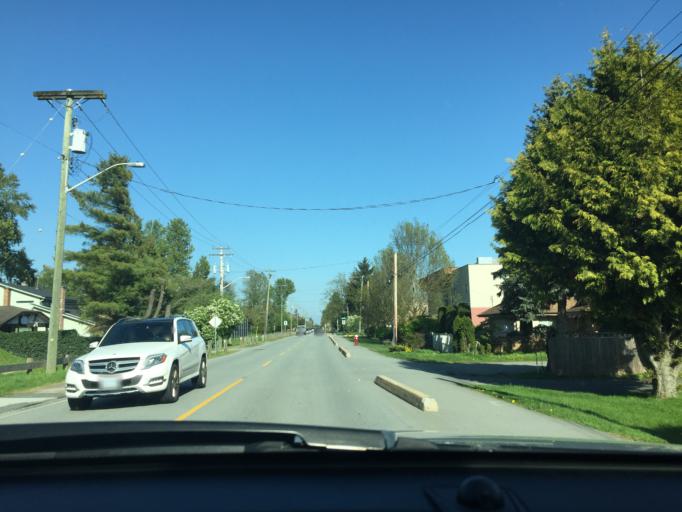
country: CA
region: British Columbia
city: Richmond
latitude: 49.1628
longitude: -123.1242
